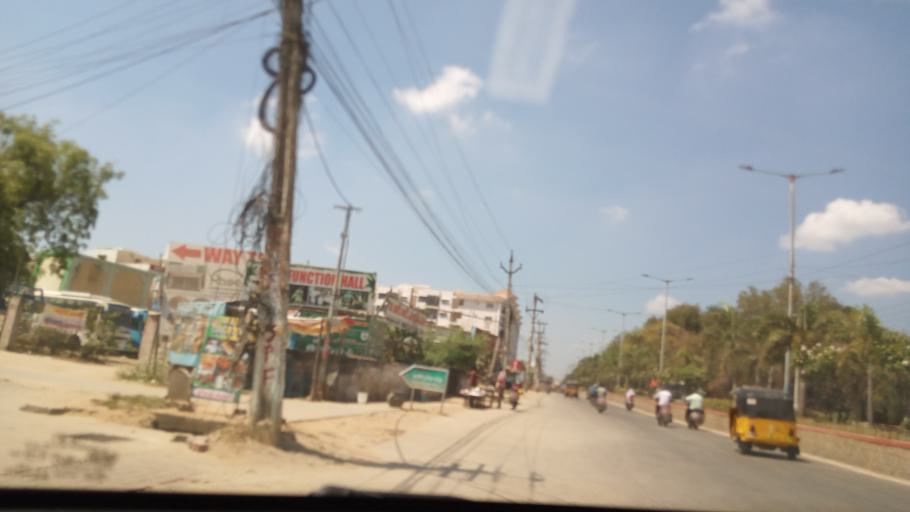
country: IN
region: Andhra Pradesh
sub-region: Chittoor
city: Akkarampalle
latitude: 13.6451
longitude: 79.4387
